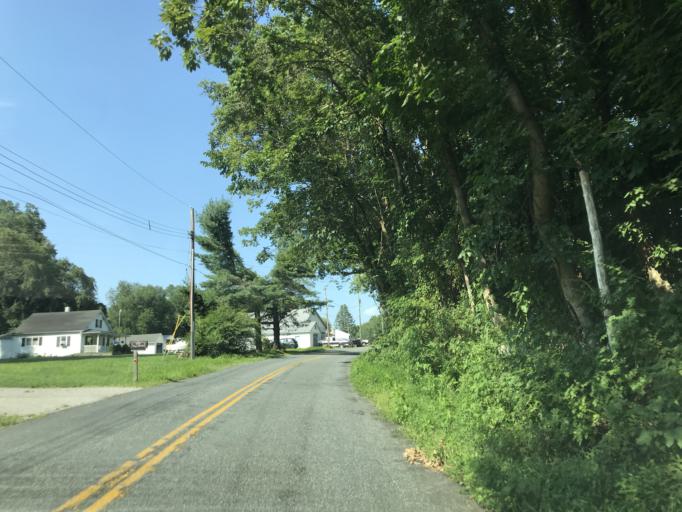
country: US
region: Maryland
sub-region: Harford County
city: South Bel Air
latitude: 39.6198
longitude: -76.2802
